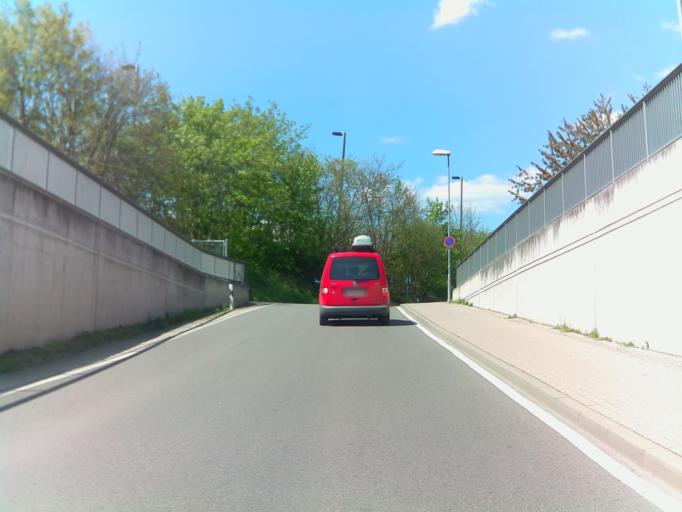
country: DE
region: Thuringia
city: Arnstadt
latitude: 50.8486
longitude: 10.9433
